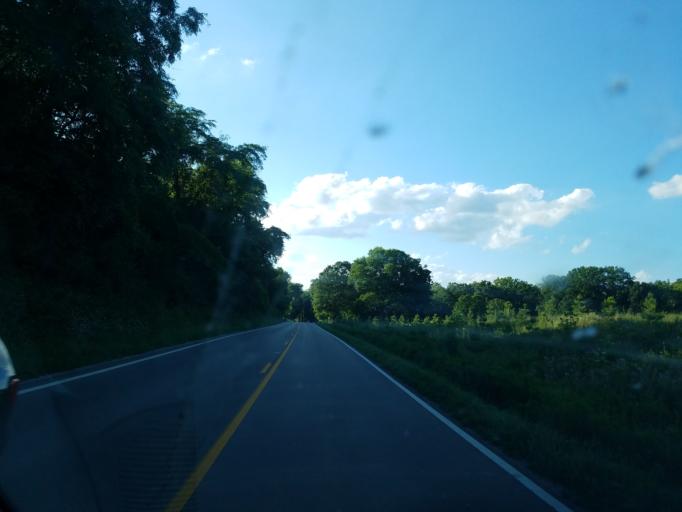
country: US
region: Ohio
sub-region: Delaware County
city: Lewis Center
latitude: 40.2030
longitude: -83.0572
